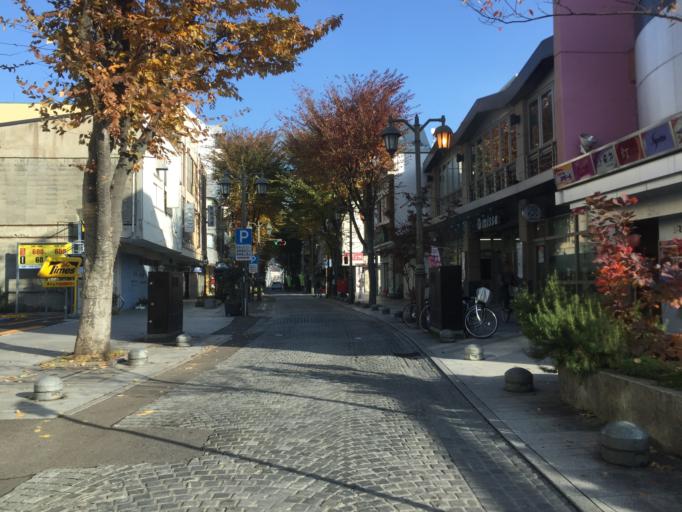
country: JP
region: Fukushima
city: Fukushima-shi
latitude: 37.7556
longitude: 140.4648
